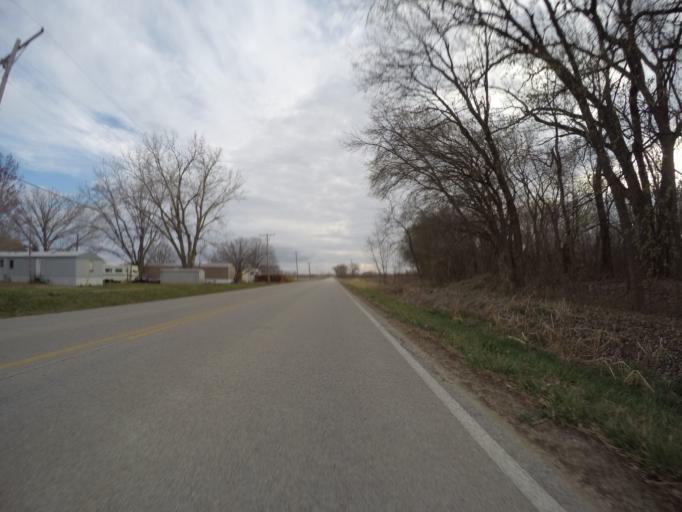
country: US
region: Kansas
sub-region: Riley County
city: Manhattan
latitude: 39.2471
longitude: -96.5702
